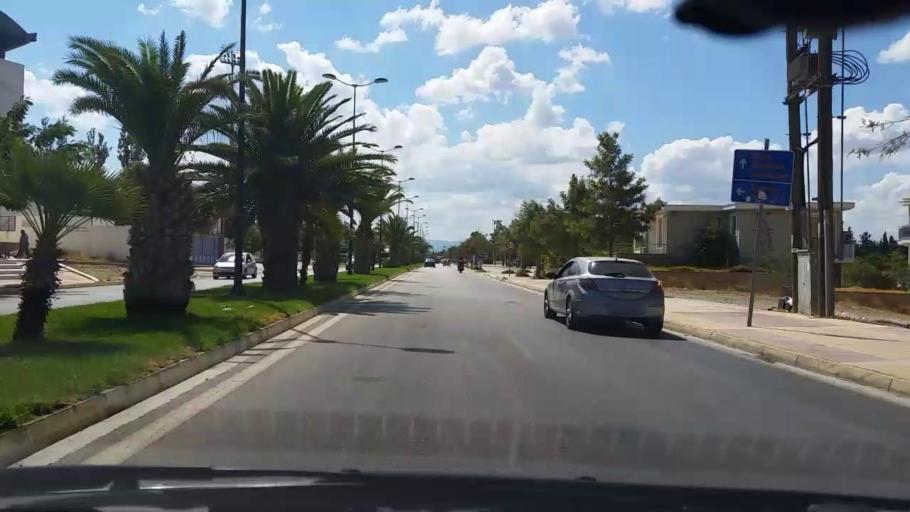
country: GR
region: Peloponnese
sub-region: Nomos Korinthias
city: Loutraki
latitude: 37.9679
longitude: 22.9782
